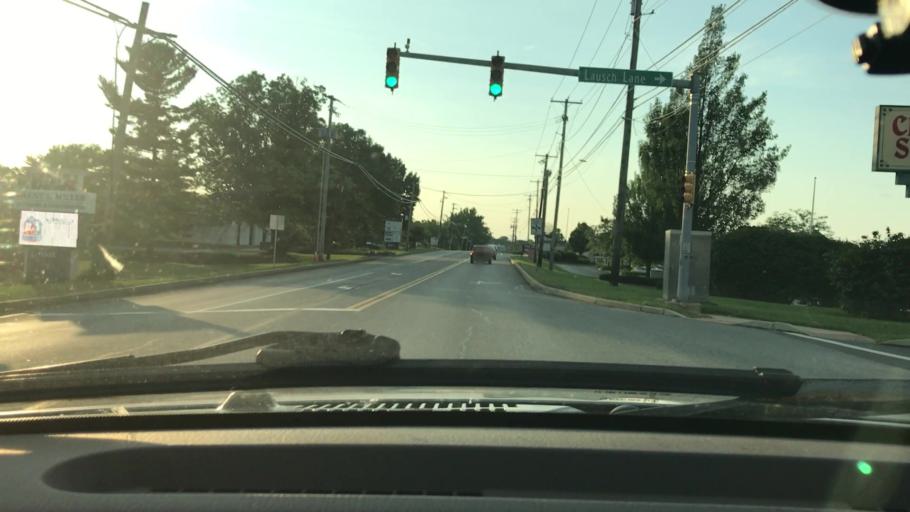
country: US
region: Pennsylvania
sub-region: Lancaster County
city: East Petersburg
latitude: 40.0815
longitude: -76.3401
